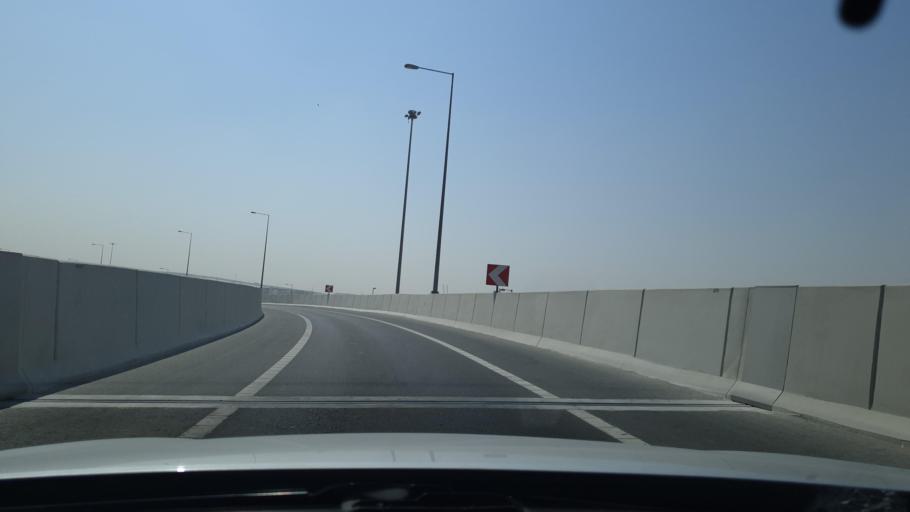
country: QA
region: Baladiyat ad Dawhah
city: Doha
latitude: 25.2210
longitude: 51.5322
